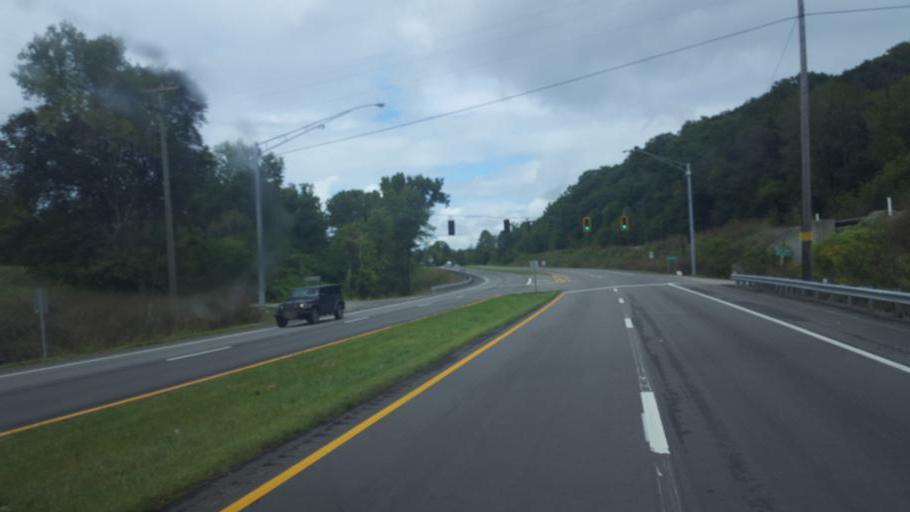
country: US
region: Ohio
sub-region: Scioto County
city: Lucasville
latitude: 38.8405
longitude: -82.9843
